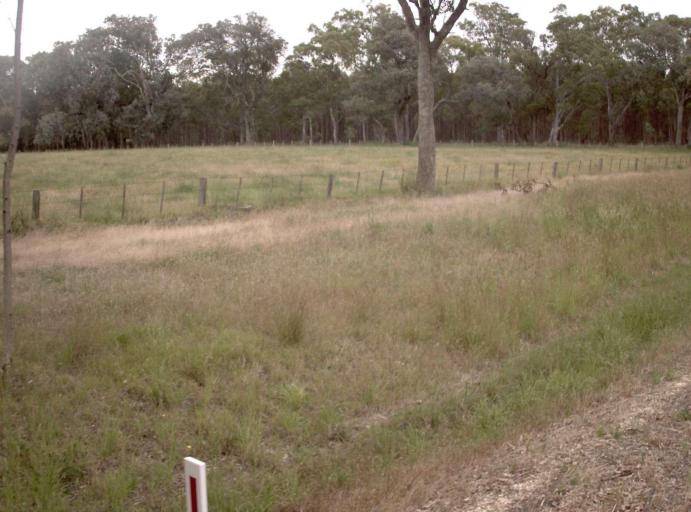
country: AU
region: Victoria
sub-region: East Gippsland
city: Bairnsdale
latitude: -37.7946
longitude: 147.3303
